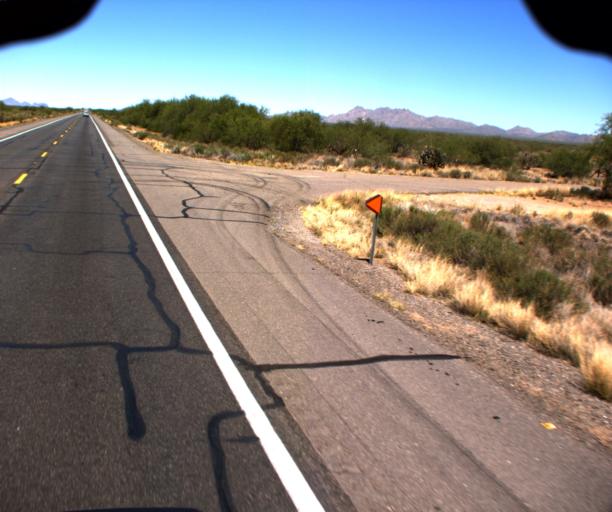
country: US
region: Arizona
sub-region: Yavapai County
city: Congress
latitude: 34.1091
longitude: -112.9299
